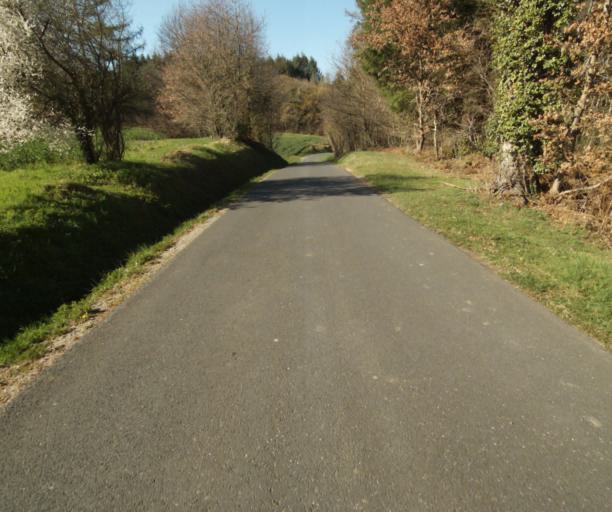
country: FR
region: Limousin
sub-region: Departement de la Correze
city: Tulle
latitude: 45.2836
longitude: 1.7212
